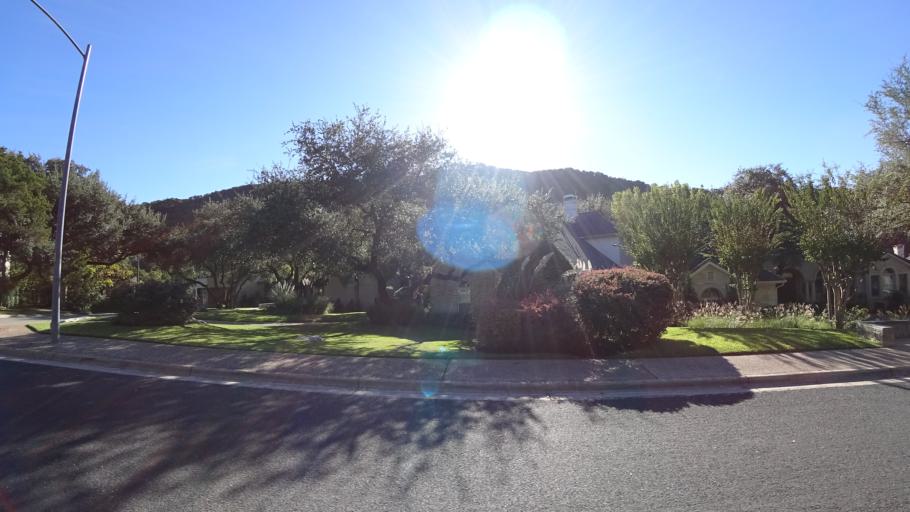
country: US
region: Texas
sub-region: Travis County
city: West Lake Hills
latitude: 30.3539
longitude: -97.7848
